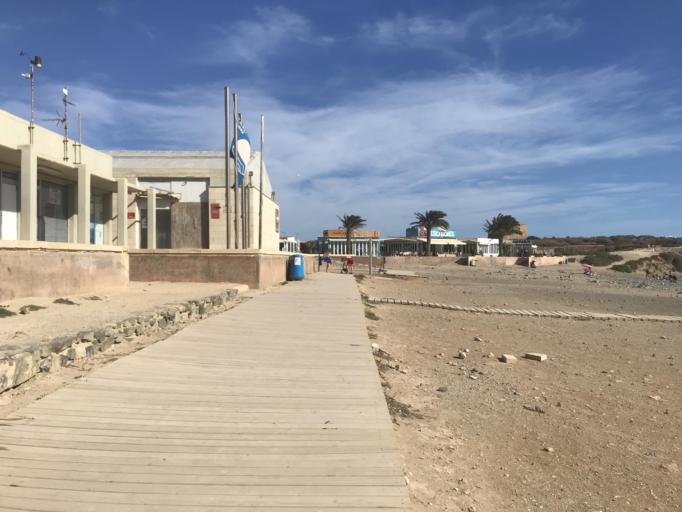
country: ES
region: Valencia
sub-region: Provincia de Alicante
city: Santa Pola
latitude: 38.1661
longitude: -0.4788
